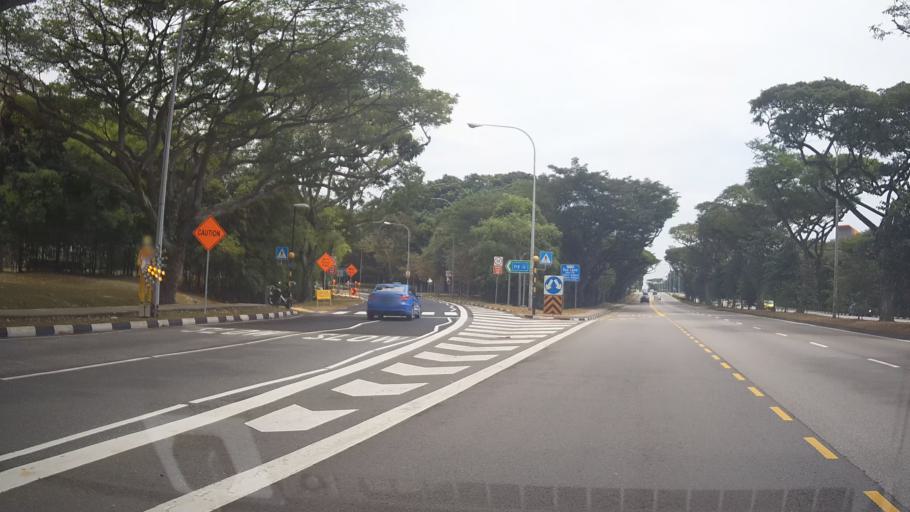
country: SG
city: Singapore
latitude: 1.3446
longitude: 103.9445
